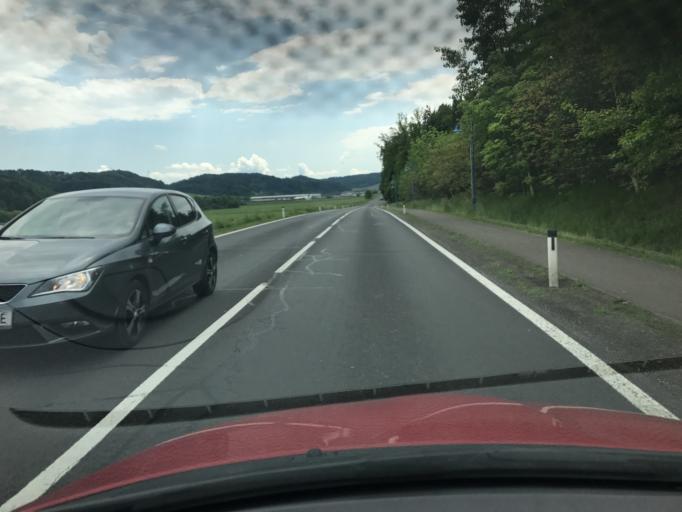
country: AT
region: Styria
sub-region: Politischer Bezirk Suedoststeiermark
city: Kirchbach in Steiermark
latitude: 46.9246
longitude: 15.6682
